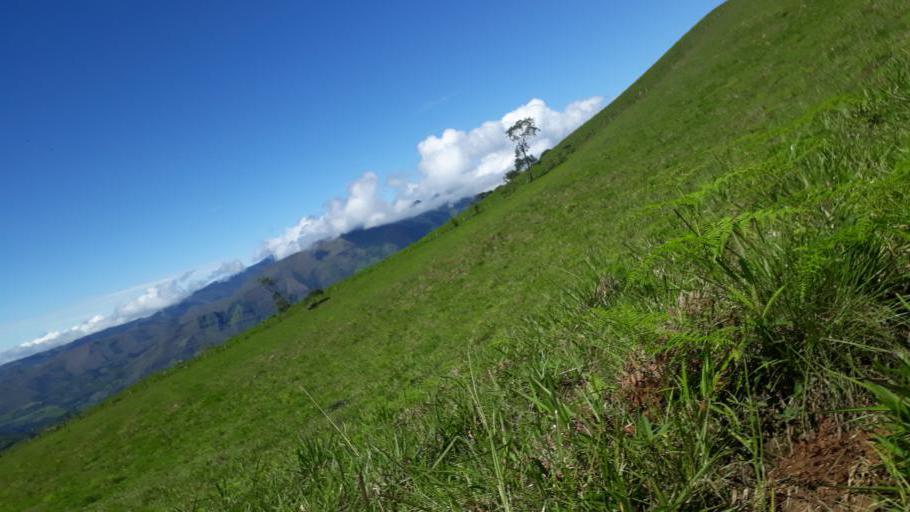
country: CO
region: Casanare
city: Nunchia
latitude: 5.6698
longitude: -72.4347
